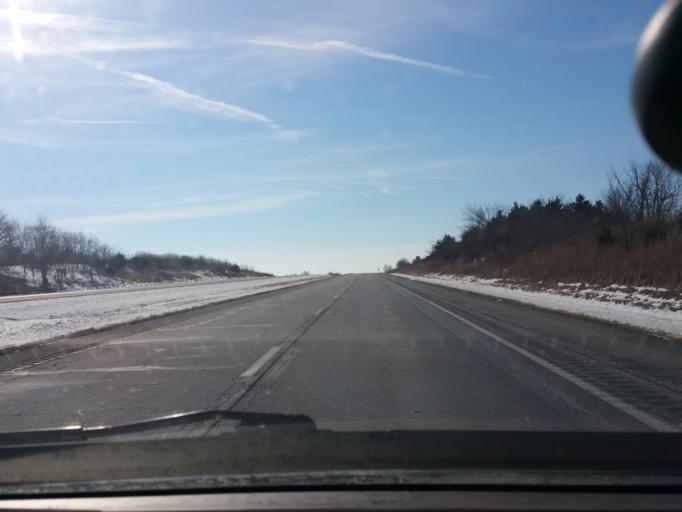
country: US
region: Missouri
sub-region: Harrison County
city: Bethany
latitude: 40.4348
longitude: -93.9861
